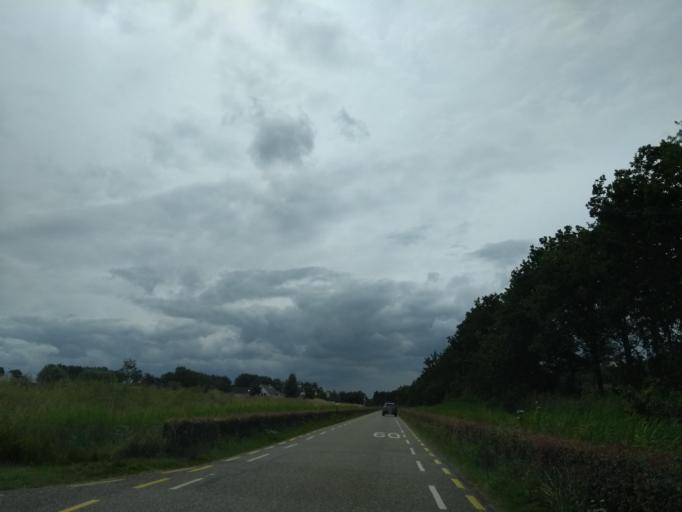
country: NL
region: Zeeland
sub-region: Gemeente Sluis
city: Sluis
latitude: 51.3908
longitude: 3.4544
